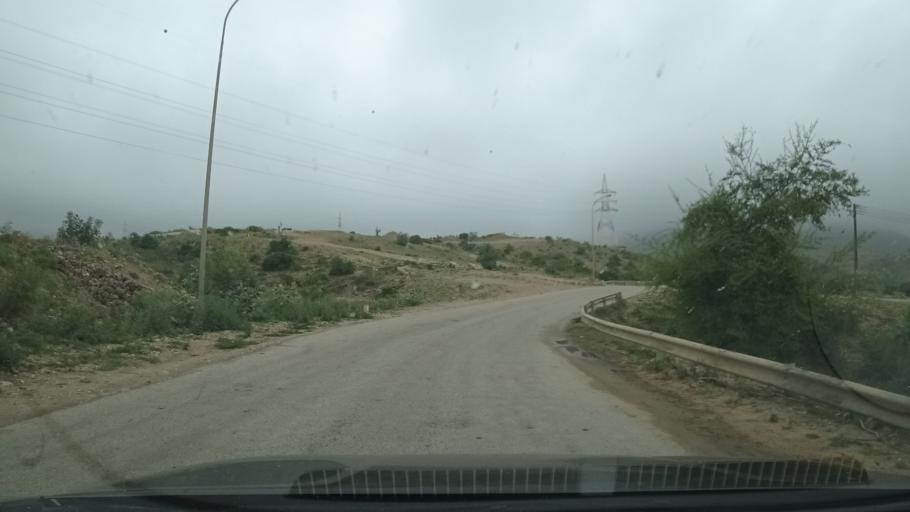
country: OM
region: Zufar
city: Salalah
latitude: 17.0921
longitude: 54.0782
